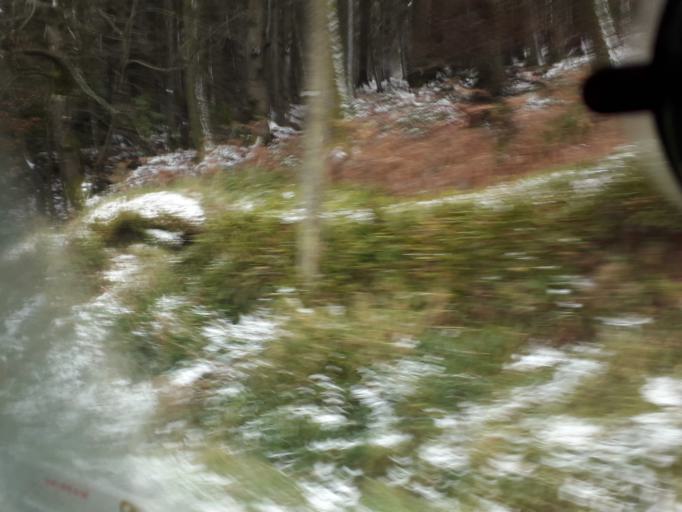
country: IE
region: Leinster
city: Ballyboden
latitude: 53.2423
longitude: -6.3102
